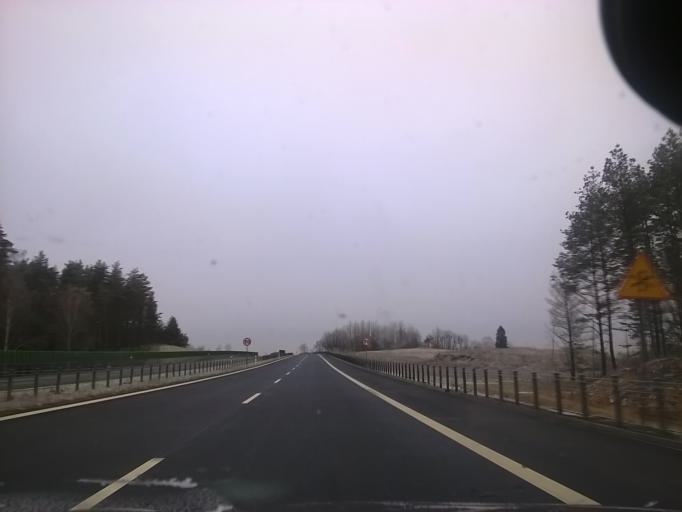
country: PL
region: Warmian-Masurian Voivodeship
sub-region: Powiat olsztynski
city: Biskupiec
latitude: 53.8456
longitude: 20.9884
